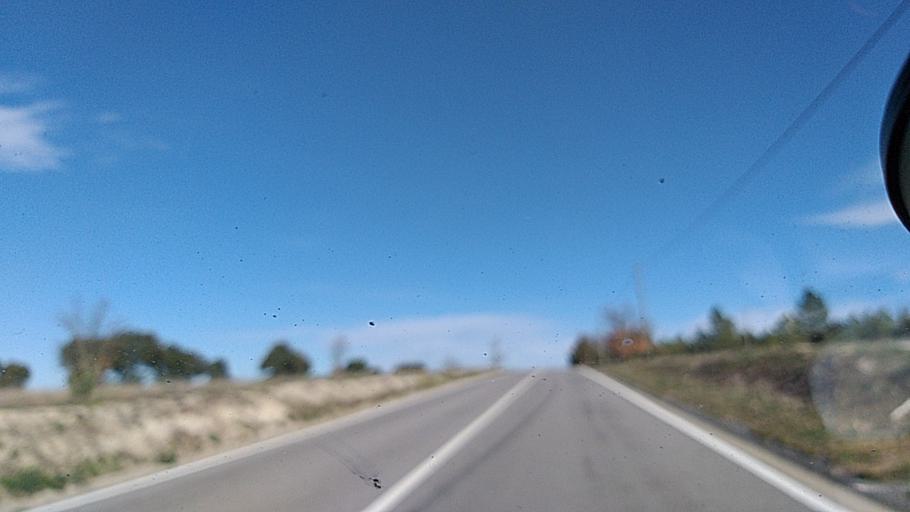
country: ES
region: Castille and Leon
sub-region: Provincia de Salamanca
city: Fuentes de Onoro
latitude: 40.6148
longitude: -6.8762
